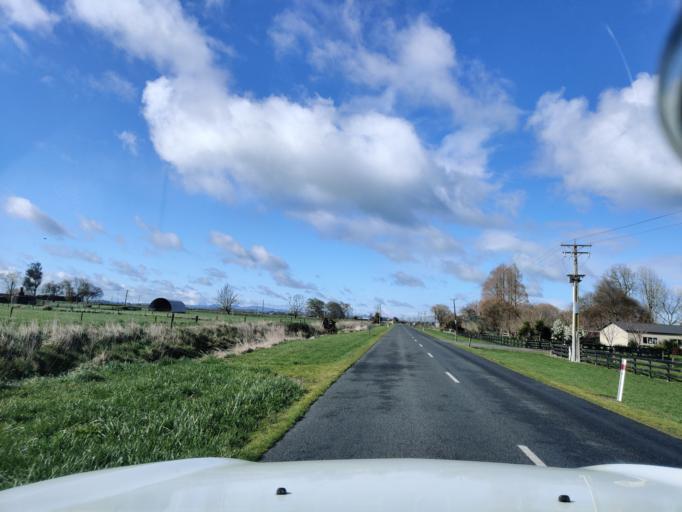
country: NZ
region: Waikato
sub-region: Hamilton City
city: Hamilton
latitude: -37.6229
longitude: 175.3210
